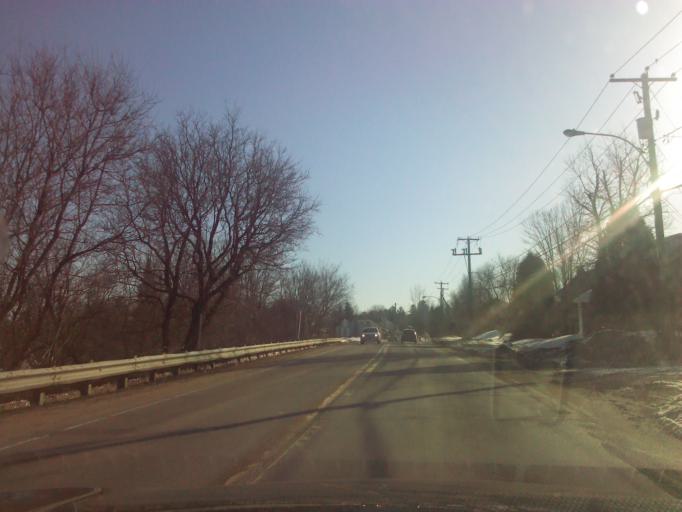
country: CA
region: Quebec
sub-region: Capitale-Nationale
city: Sainte Catherine de la Jacques Cartier
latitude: 46.8448
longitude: -71.6135
